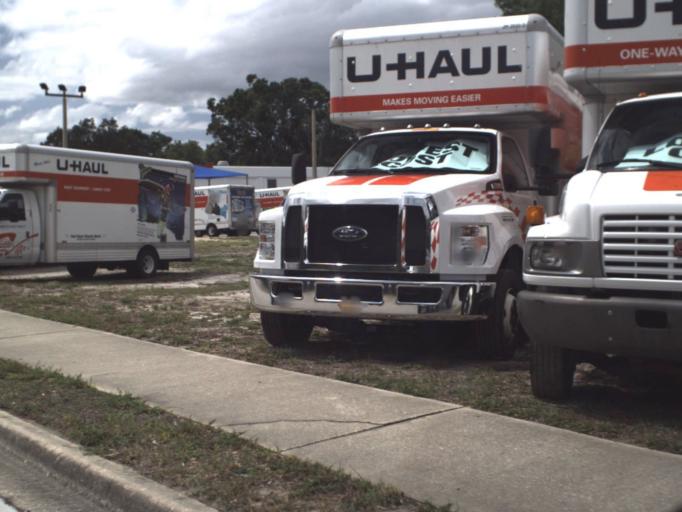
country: US
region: Florida
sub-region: Brevard County
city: Titusville
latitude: 28.6154
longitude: -80.8260
